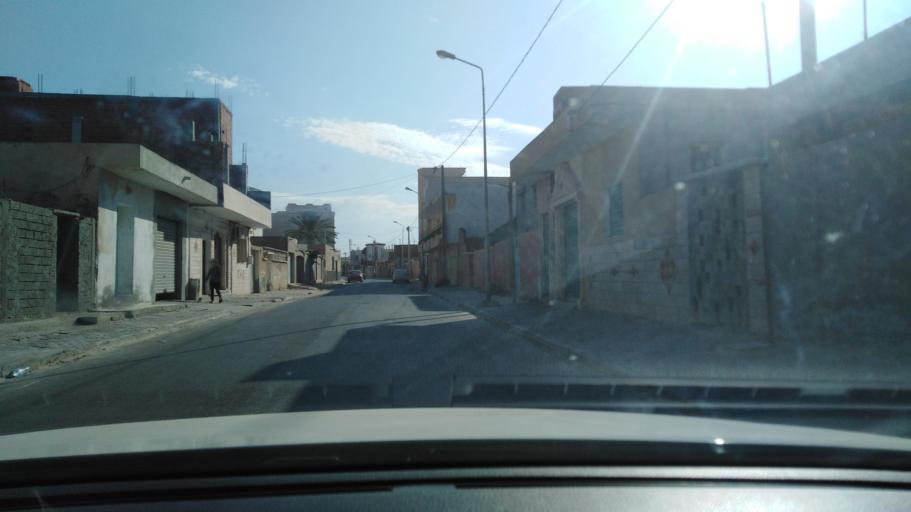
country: TN
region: Qabis
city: Gabes
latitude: 33.9406
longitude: 10.0724
